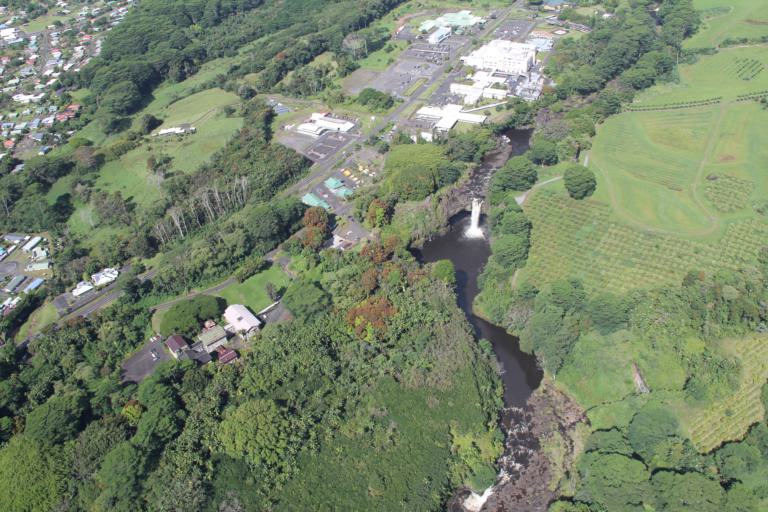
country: US
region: Hawaii
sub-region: Hawaii County
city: Hilo
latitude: 19.7174
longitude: -155.1062
